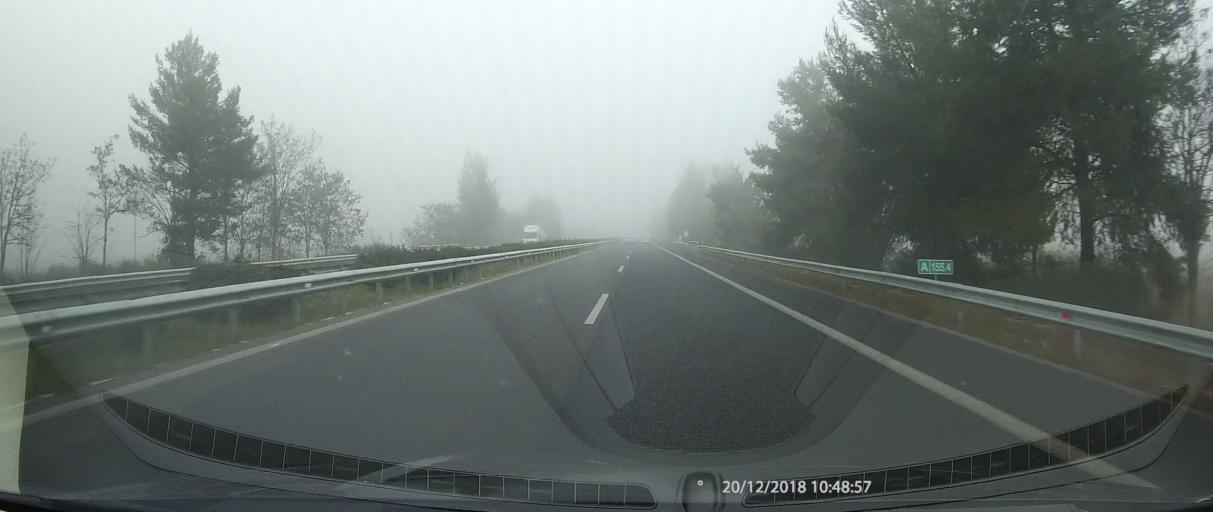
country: GR
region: Peloponnese
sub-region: Nomos Arkadias
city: Tripoli
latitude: 37.5281
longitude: 22.4105
